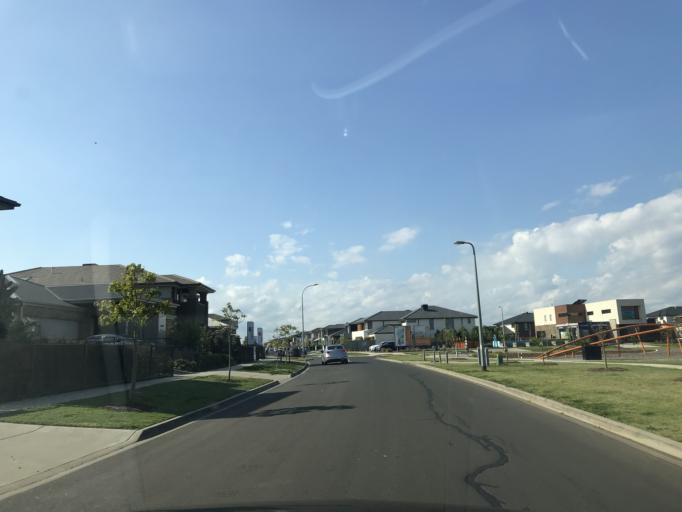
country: AU
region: Victoria
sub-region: Wyndham
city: Hoppers Crossing
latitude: -37.8946
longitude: 144.7149
